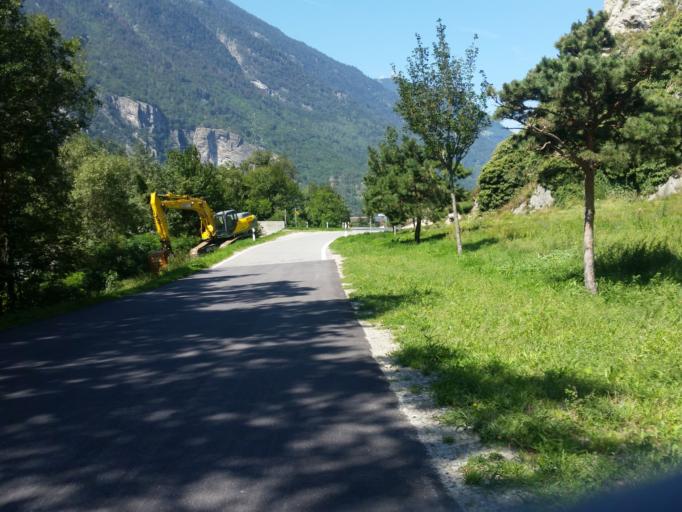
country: CH
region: Valais
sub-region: Saint-Maurice District
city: Vernayaz
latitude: 46.1426
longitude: 7.0467
